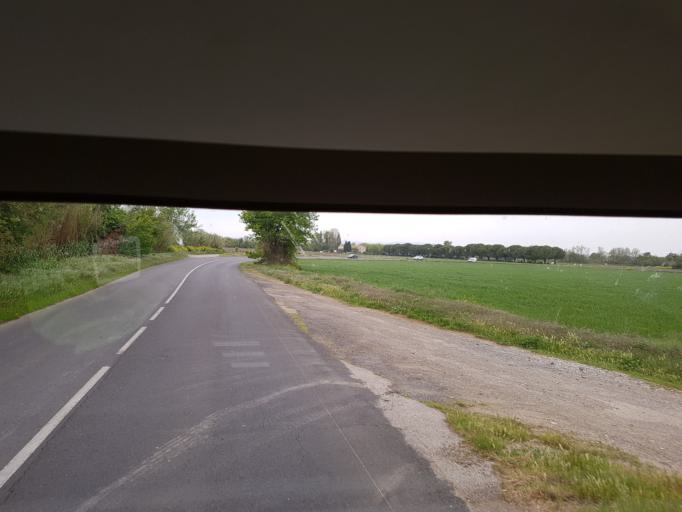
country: FR
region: Languedoc-Roussillon
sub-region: Departement de l'Herault
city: Serignan
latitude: 43.2951
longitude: 3.2769
